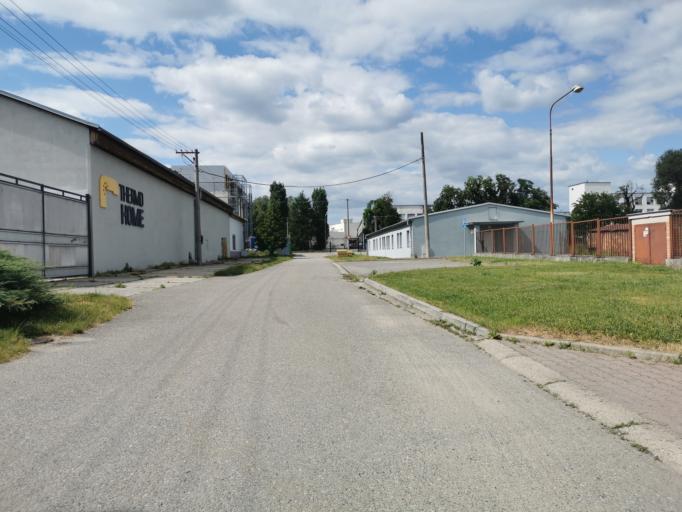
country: CZ
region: South Moravian
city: Rohatec
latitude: 48.8876
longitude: 17.2089
